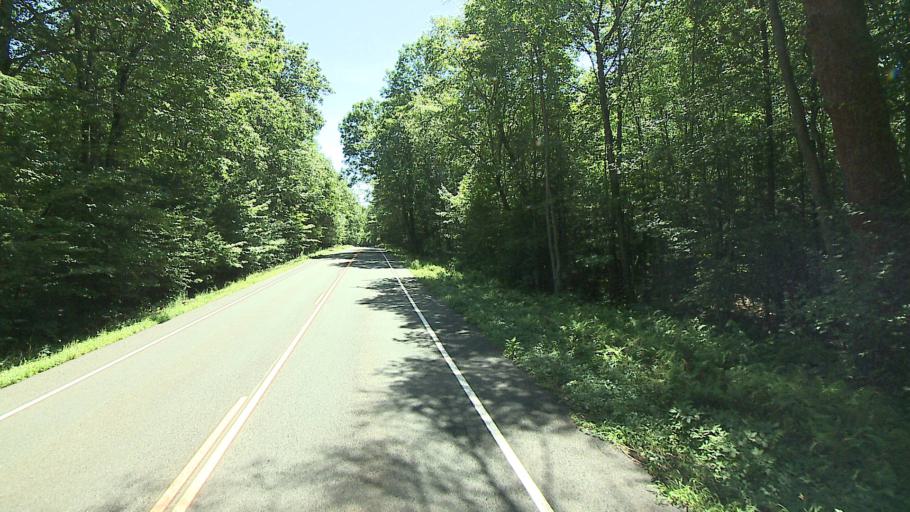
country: US
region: Connecticut
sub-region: Litchfield County
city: New Hartford Center
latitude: 41.9683
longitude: -72.9801
